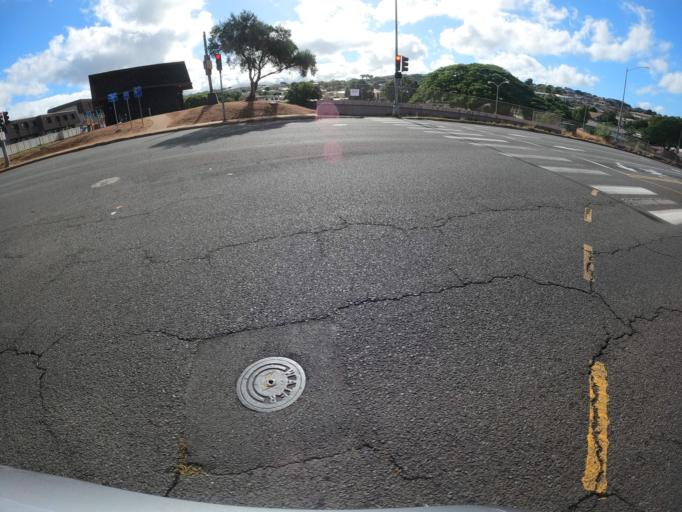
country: US
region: Hawaii
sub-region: Honolulu County
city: Halawa
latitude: 21.3570
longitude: -157.9266
